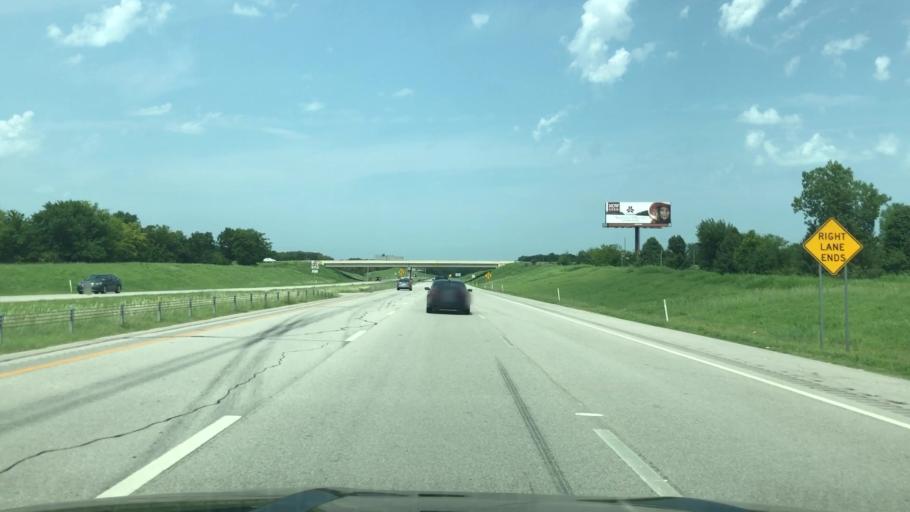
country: US
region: Oklahoma
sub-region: Rogers County
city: Catoosa
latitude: 36.1741
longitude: -95.7319
